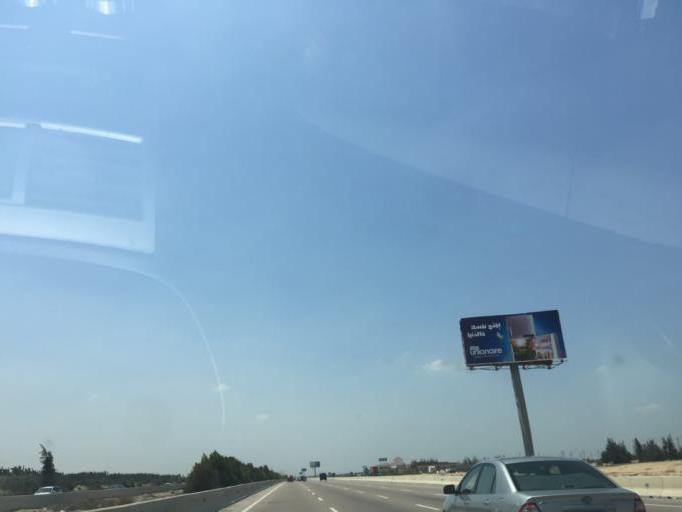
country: EG
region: Al Buhayrah
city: Beheira
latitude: 30.4490
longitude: 30.3177
